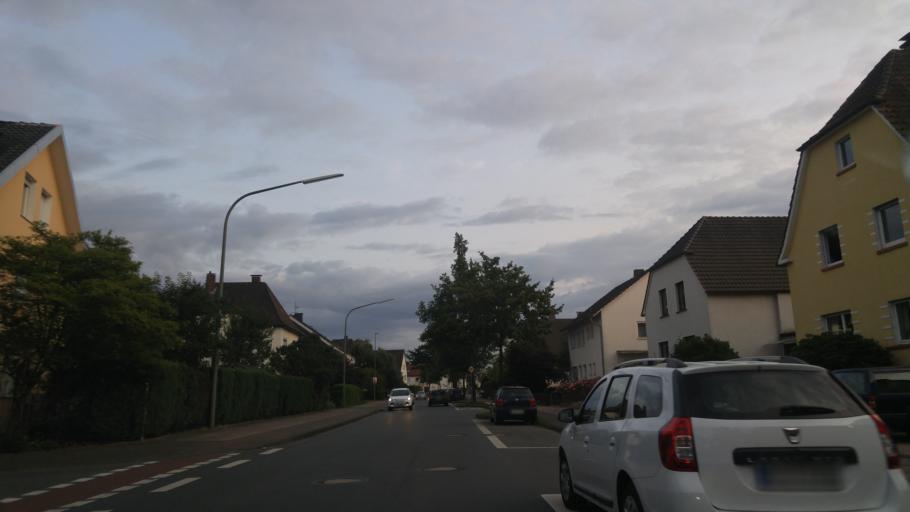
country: DE
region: North Rhine-Westphalia
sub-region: Regierungsbezirk Detmold
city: Bielefeld
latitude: 52.0527
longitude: 8.5274
